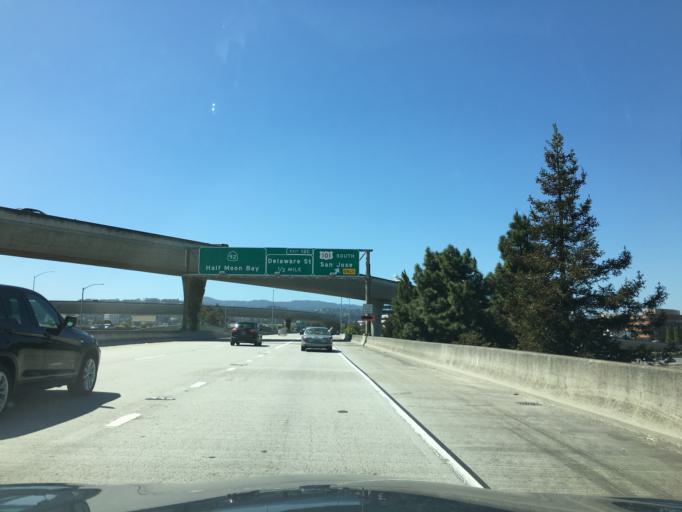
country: US
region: California
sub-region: San Mateo County
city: Foster City
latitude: 37.5538
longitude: -122.2943
